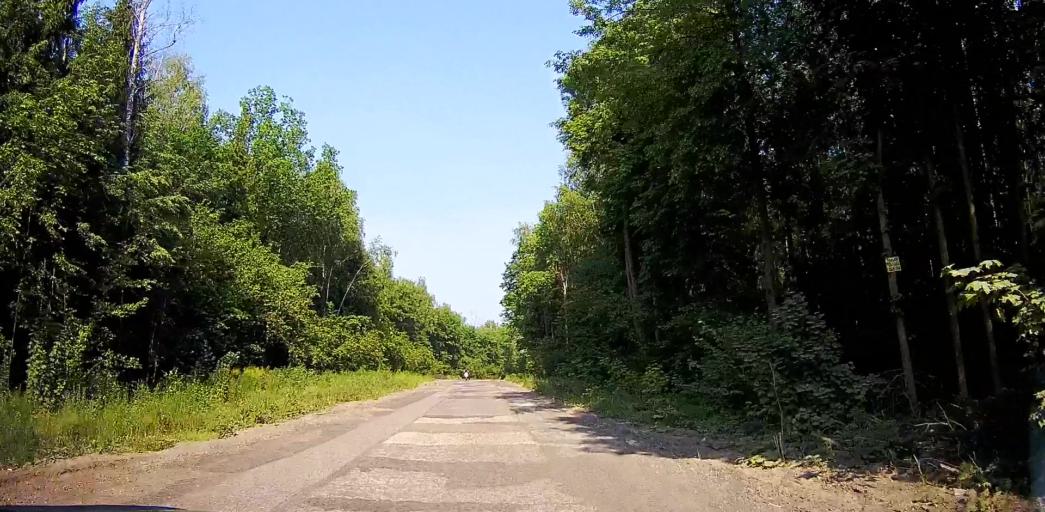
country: RU
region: Moskovskaya
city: Yakovlevskoye
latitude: 55.4314
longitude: 37.9179
